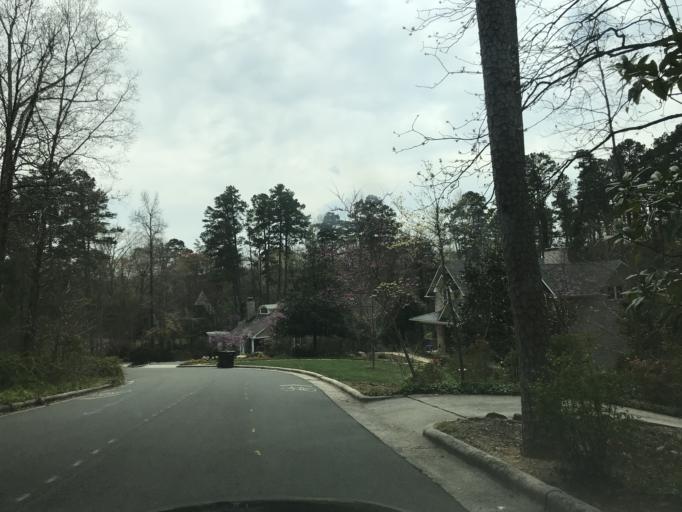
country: US
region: North Carolina
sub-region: Orange County
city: Chapel Hill
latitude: 35.9026
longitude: -79.0355
